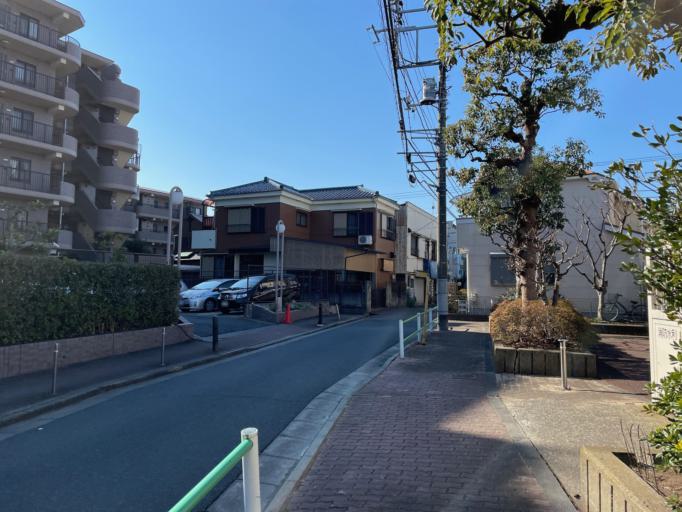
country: JP
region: Saitama
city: Soka
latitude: 35.7974
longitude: 139.7823
